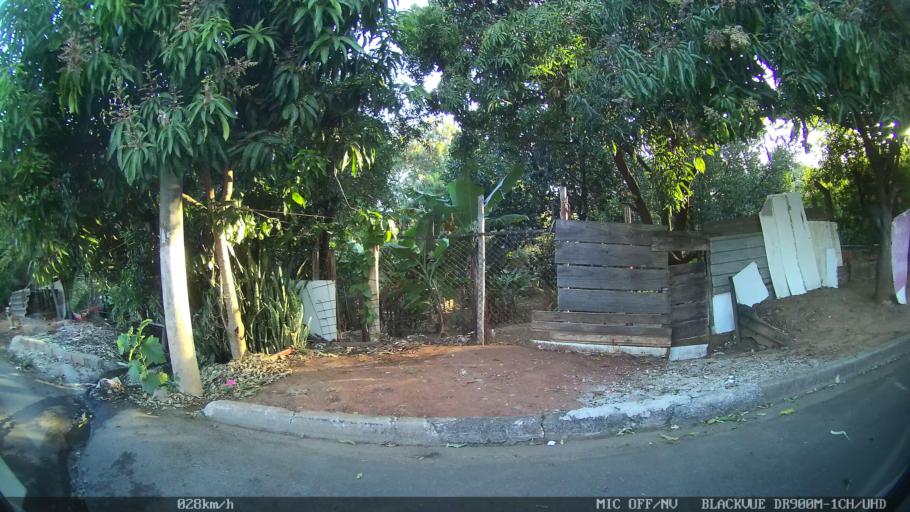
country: BR
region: Sao Paulo
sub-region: Santa Barbara D'Oeste
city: Santa Barbara d'Oeste
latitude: -22.7488
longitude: -47.3827
